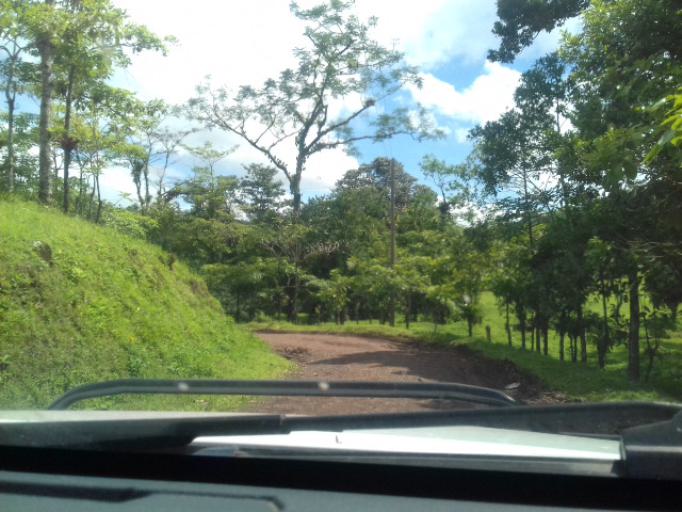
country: NI
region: Matagalpa
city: Rio Blanco
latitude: 12.9889
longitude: -85.1891
